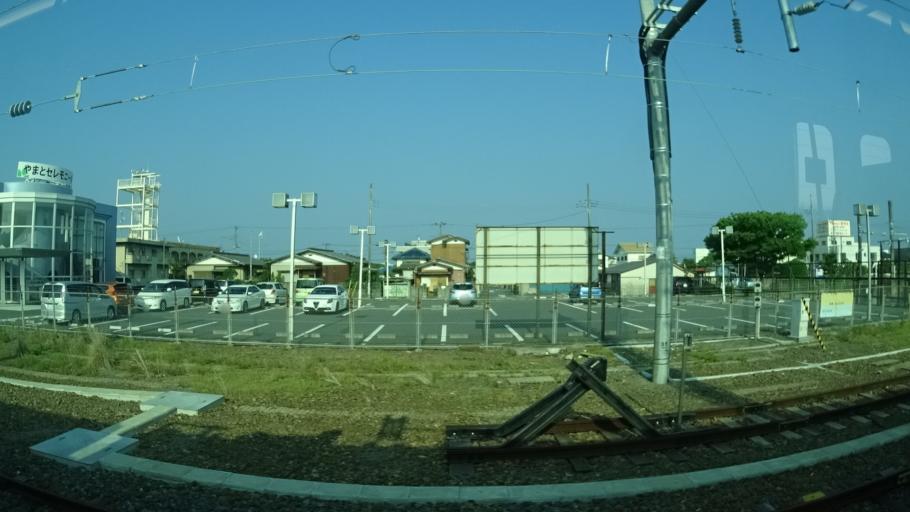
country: JP
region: Ibaraki
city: Takahagi
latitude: 36.7160
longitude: 140.7175
